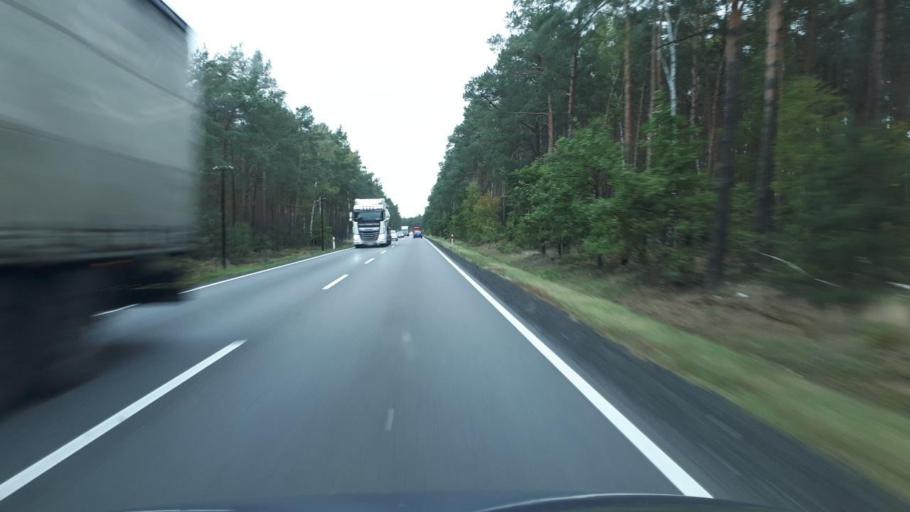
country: PL
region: Greater Poland Voivodeship
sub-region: Powiat ostrzeszowski
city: Ostrzeszow
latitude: 51.4733
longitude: 17.8908
